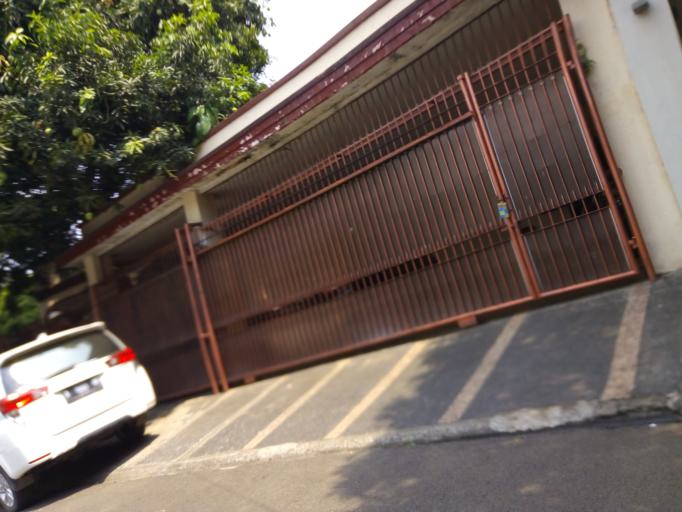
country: ID
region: Jakarta Raya
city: Jakarta
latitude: -6.2040
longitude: 106.8415
